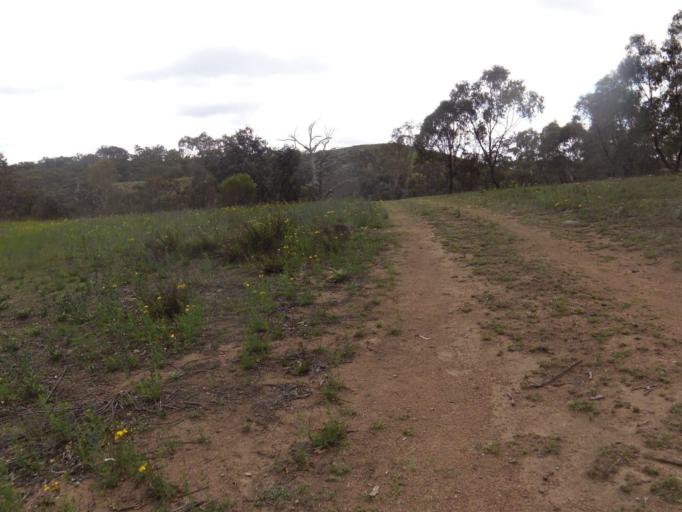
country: AU
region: Australian Capital Territory
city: Forrest
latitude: -35.3497
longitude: 149.1228
